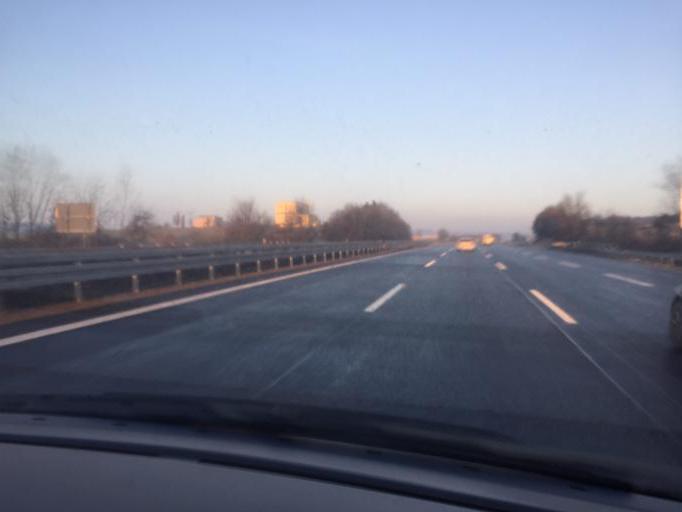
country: DE
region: Baden-Wuerttemberg
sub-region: Freiburg Region
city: Engen
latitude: 47.8596
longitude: 8.7905
